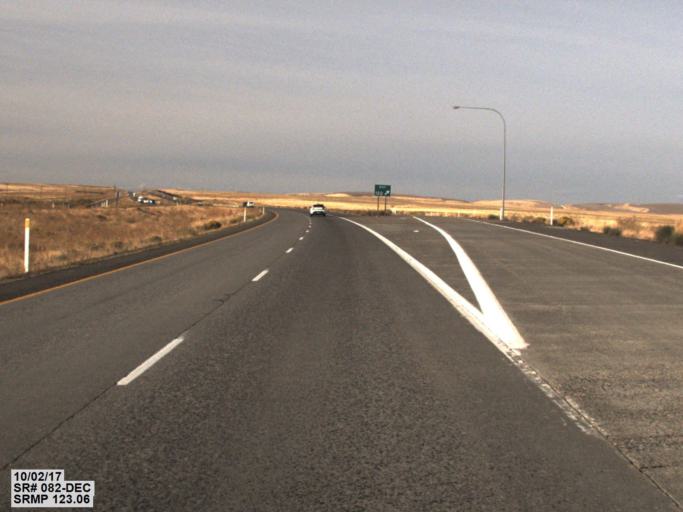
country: US
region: Oregon
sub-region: Umatilla County
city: Umatilla
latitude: 46.0209
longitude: -119.2251
